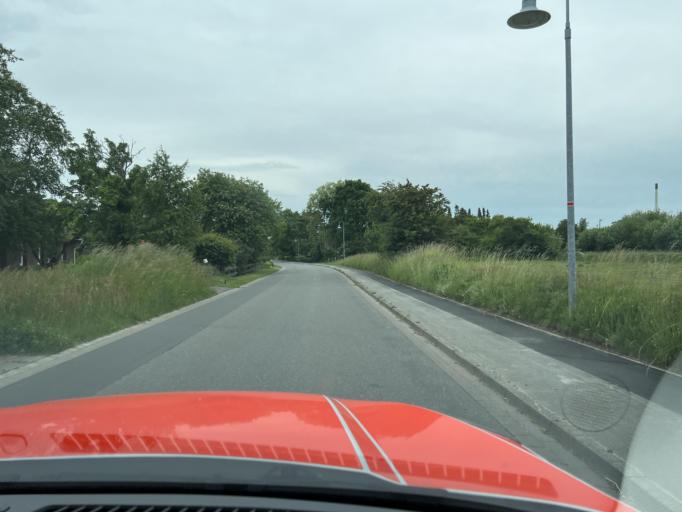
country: DE
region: Schleswig-Holstein
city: Heide
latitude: 54.1663
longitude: 9.0923
